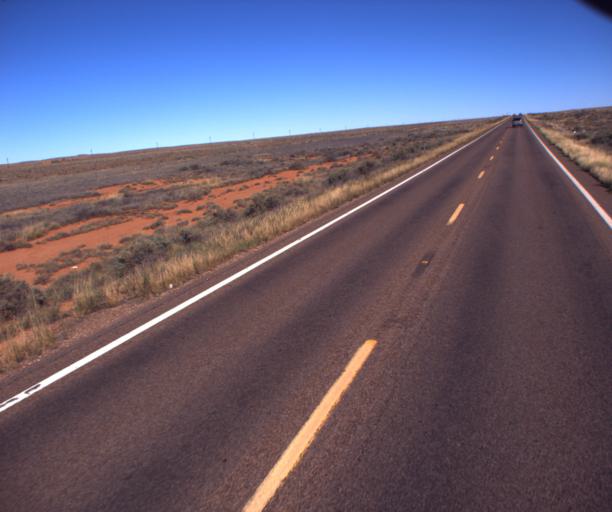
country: US
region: Arizona
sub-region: Navajo County
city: Holbrook
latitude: 34.7771
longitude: -110.1291
